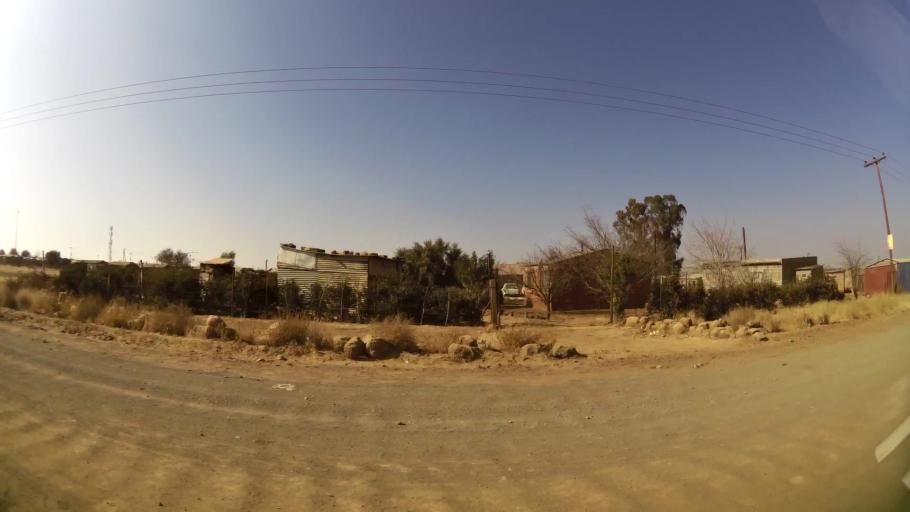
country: ZA
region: Orange Free State
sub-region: Mangaung Metropolitan Municipality
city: Bloemfontein
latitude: -29.1874
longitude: 26.2846
